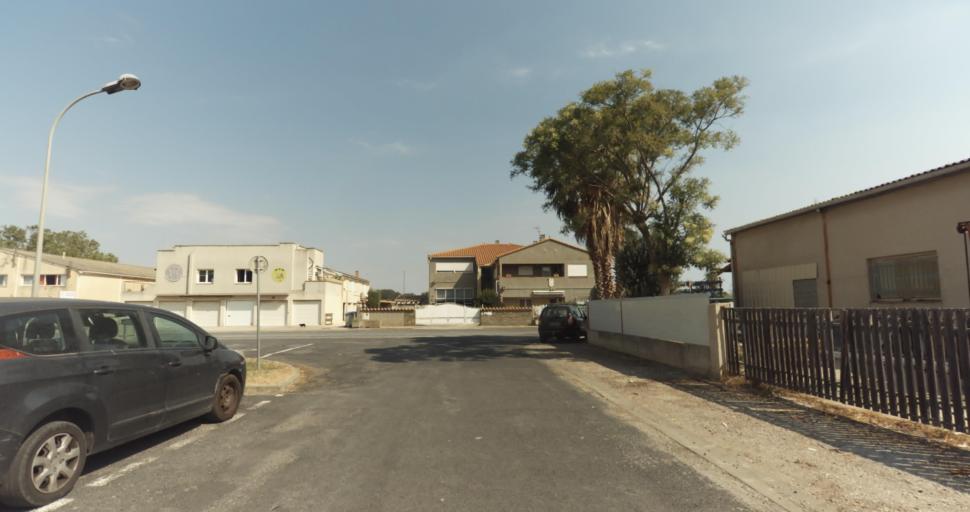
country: FR
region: Languedoc-Roussillon
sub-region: Departement des Pyrenees-Orientales
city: Saint-Cyprien-Plage
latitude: 42.6136
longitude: 3.0308
